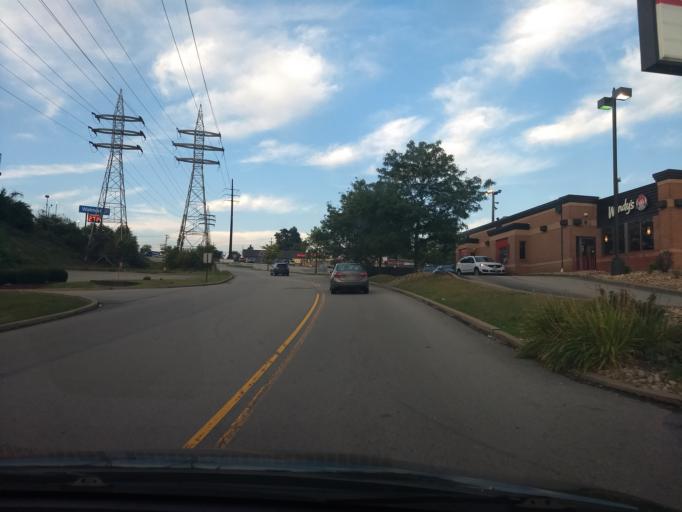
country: US
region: Pennsylvania
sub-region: Allegheny County
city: Wilmerding
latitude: 40.3848
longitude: -79.8233
